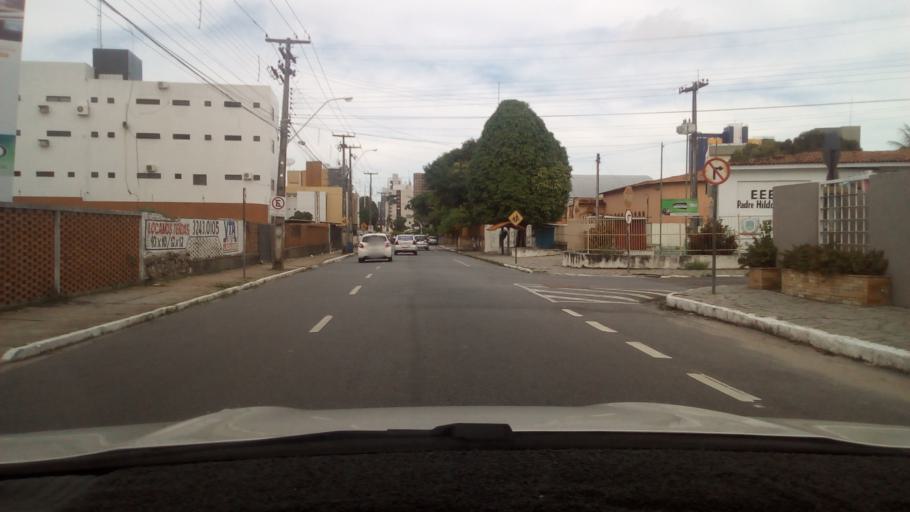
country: BR
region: Paraiba
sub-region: Joao Pessoa
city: Joao Pessoa
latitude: -7.1211
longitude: -34.8609
